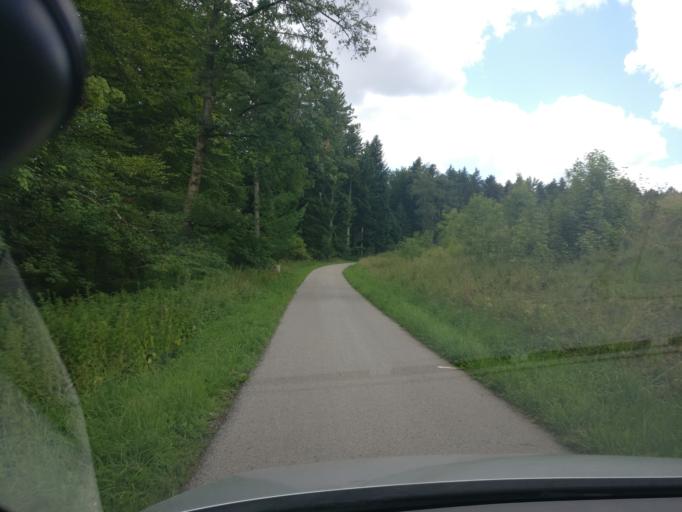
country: DE
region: Baden-Wuerttemberg
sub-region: Karlsruhe Region
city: Lossburg
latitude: 48.4075
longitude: 8.4249
